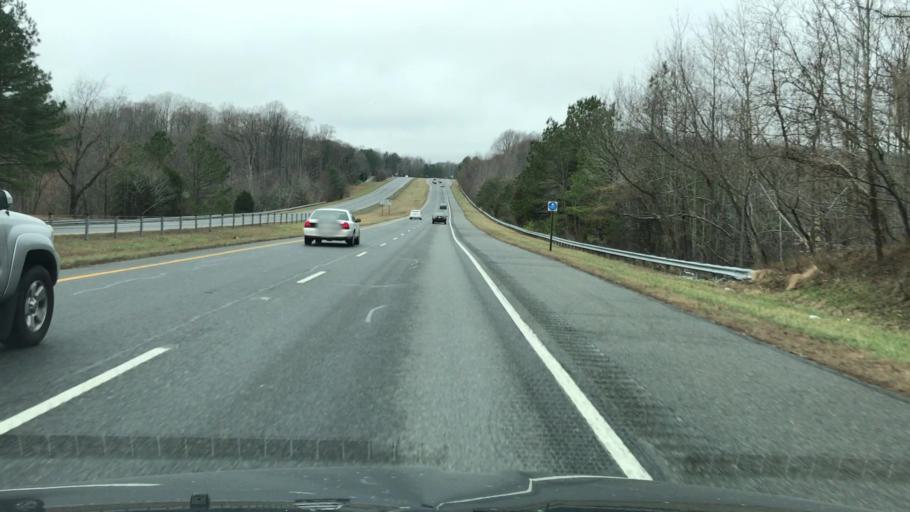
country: US
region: Maryland
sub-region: Calvert County
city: Long Beach
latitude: 38.4463
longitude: -76.4789
